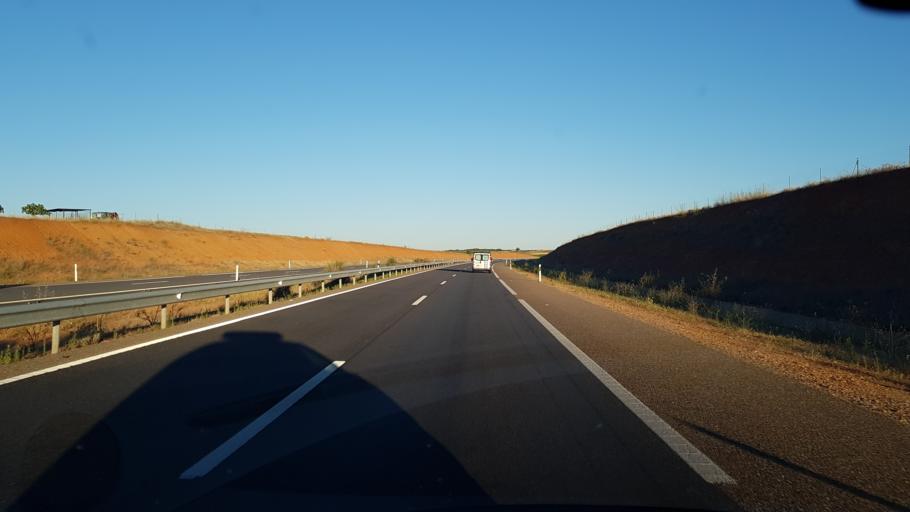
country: ES
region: Castille and Leon
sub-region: Provincia de Zamora
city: Morales de Toro
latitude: 41.5263
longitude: -5.2577
